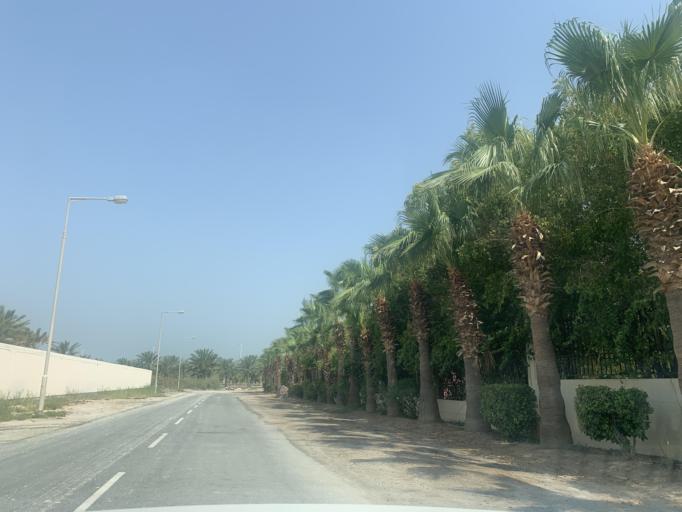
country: BH
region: Central Governorate
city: Madinat Hamad
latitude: 26.1711
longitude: 50.4571
